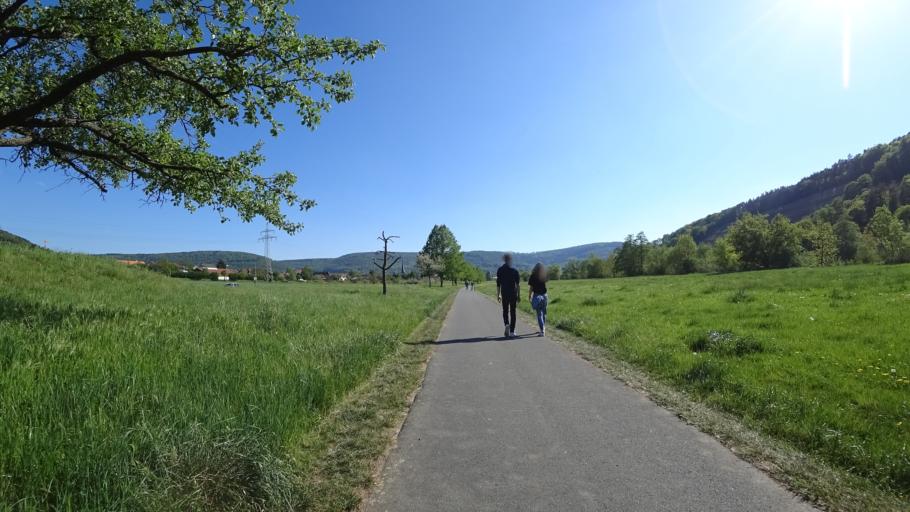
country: DE
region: Bavaria
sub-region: Regierungsbezirk Unterfranken
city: Burgstadt
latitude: 49.7231
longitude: 9.2672
